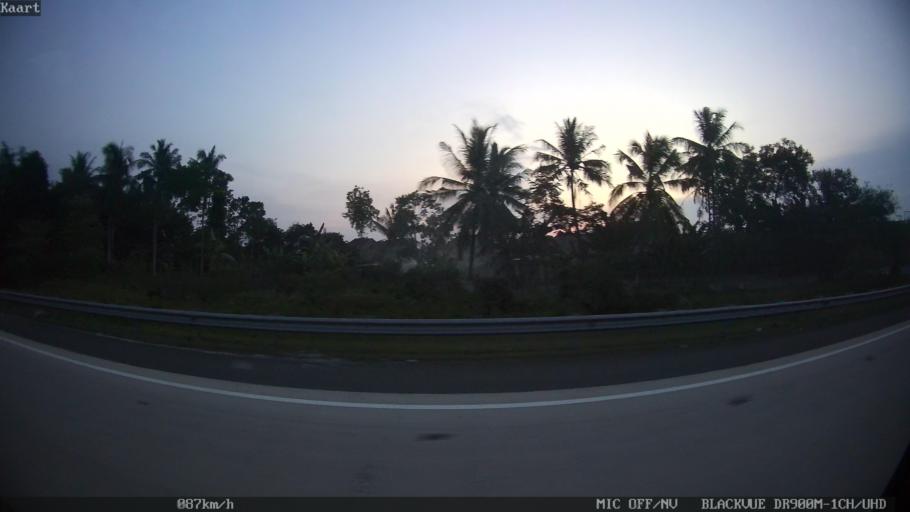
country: ID
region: Lampung
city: Sidorejo
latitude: -5.6348
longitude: 105.5688
